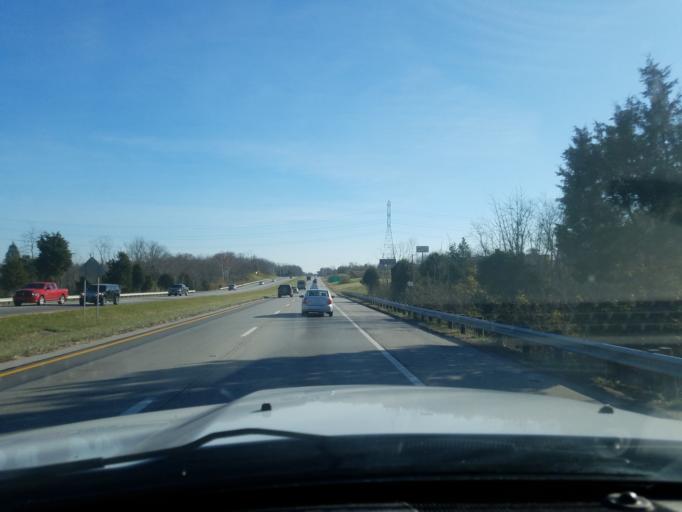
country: US
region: Ohio
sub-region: Clermont County
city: Summerside
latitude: 39.0887
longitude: -84.2332
